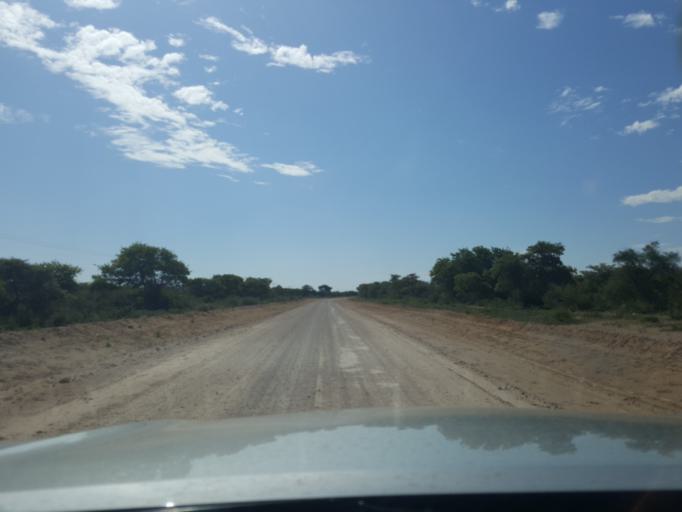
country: BW
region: Kweneng
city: Khudumelapye
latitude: -23.7933
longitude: 24.7918
